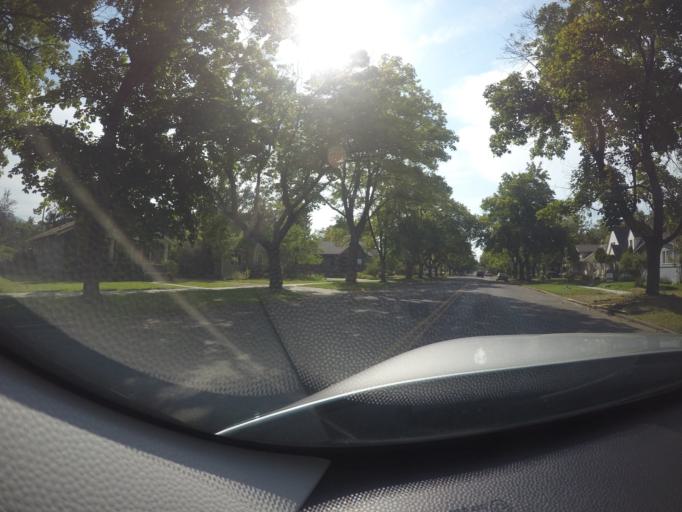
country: US
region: Montana
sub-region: Missoula County
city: Missoula
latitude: 46.8571
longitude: -113.9898
